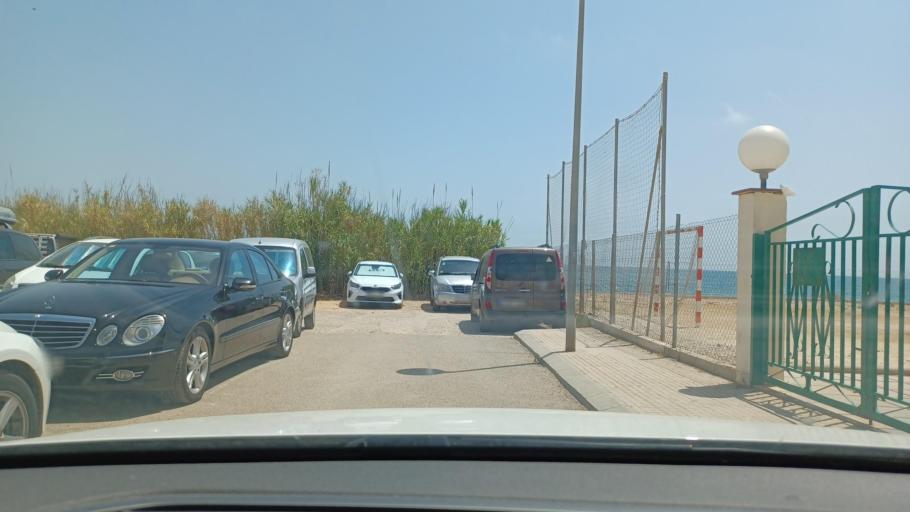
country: ES
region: Catalonia
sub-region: Provincia de Tarragona
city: Alcanar
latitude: 40.5601
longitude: 0.5343
